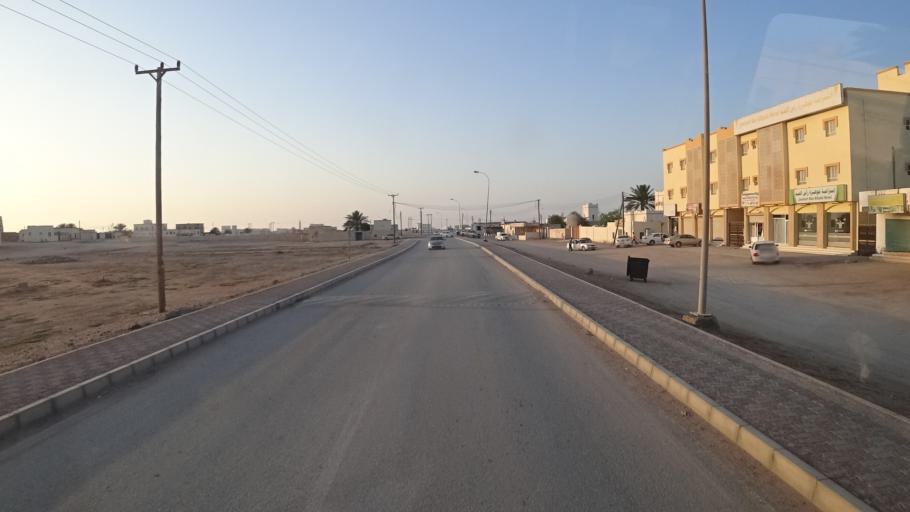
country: OM
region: Ash Sharqiyah
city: Sur
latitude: 22.5230
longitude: 59.7921
